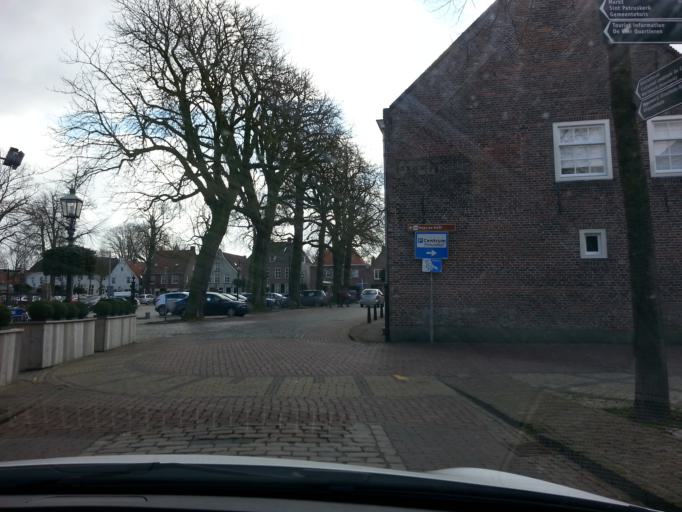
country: NL
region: North Brabant
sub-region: Gemeente Oirschot
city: Oirschot
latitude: 51.5034
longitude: 5.3063
